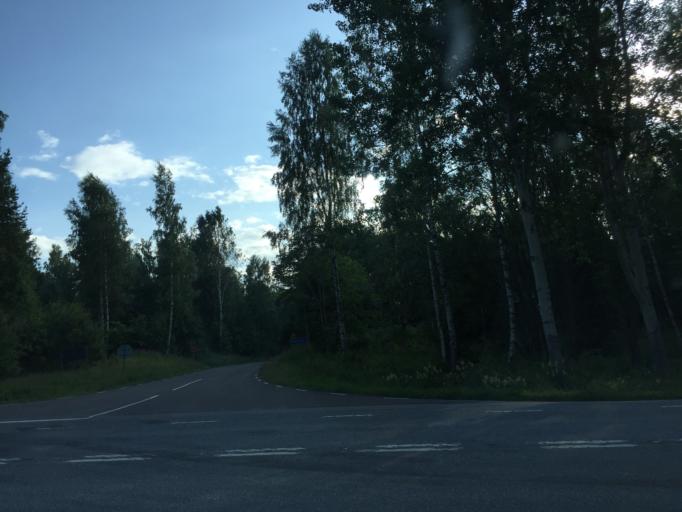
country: SE
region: OEstergoetland
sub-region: Motala Kommun
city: Ryd
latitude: 58.6773
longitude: 14.9647
